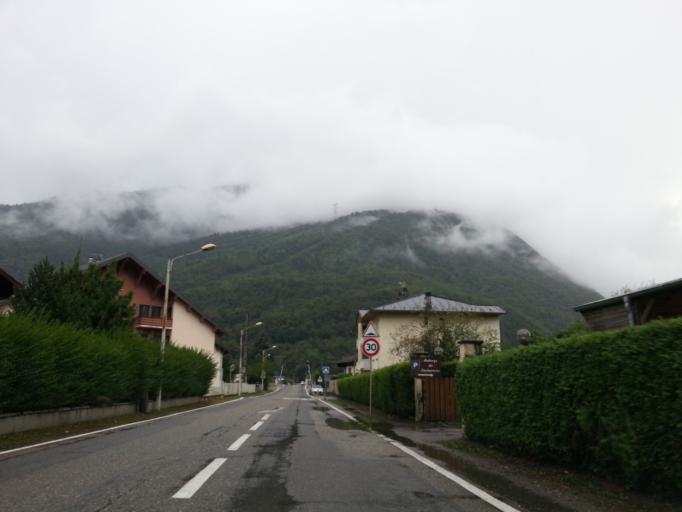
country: FR
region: Rhone-Alpes
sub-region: Departement de la Savoie
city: Albertville
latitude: 45.6678
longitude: 6.3948
